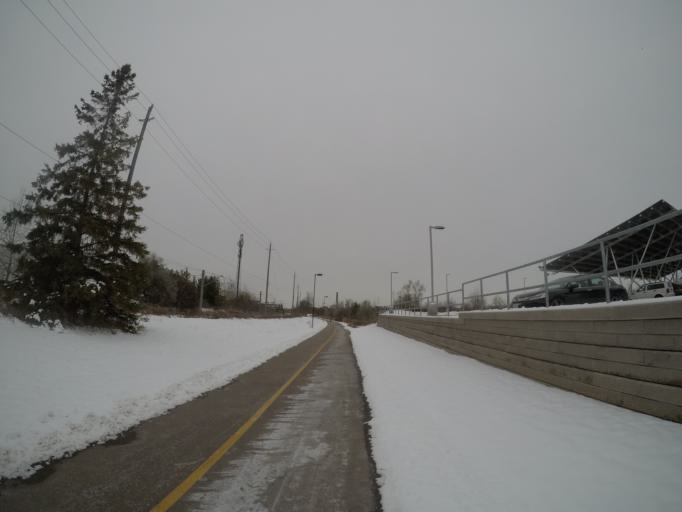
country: CA
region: Ontario
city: Waterloo
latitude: 43.4808
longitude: -80.5454
